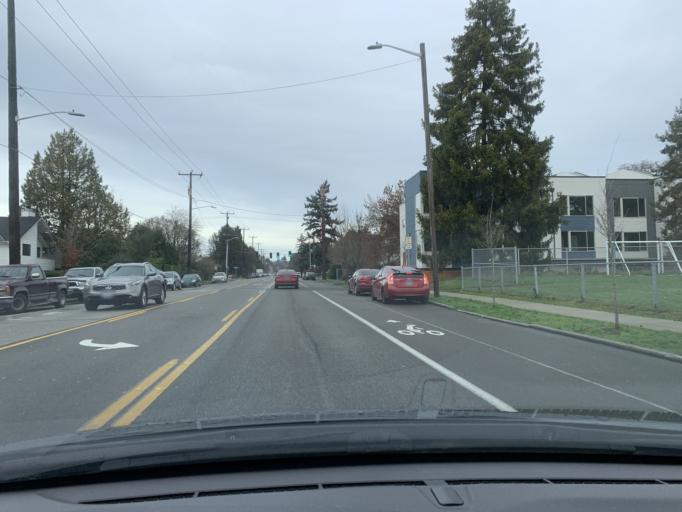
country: US
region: Washington
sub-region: King County
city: White Center
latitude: 47.5545
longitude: -122.3816
